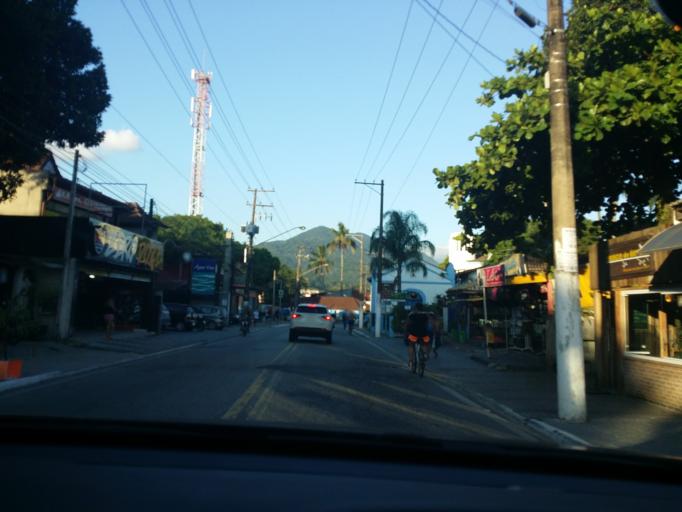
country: BR
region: Sao Paulo
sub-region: Sao Sebastiao
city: Sao Sebastiao
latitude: -23.7846
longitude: -45.6235
